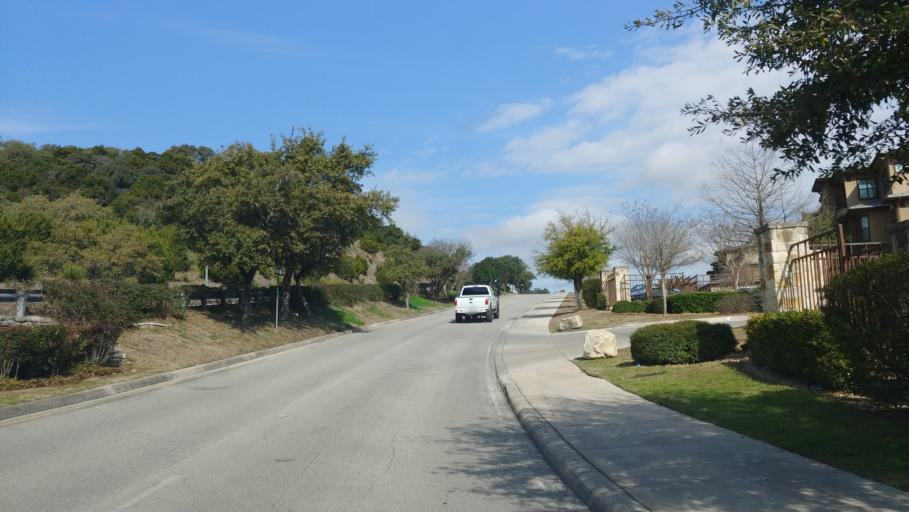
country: US
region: Texas
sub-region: Bexar County
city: Cross Mountain
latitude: 29.6216
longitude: -98.6122
